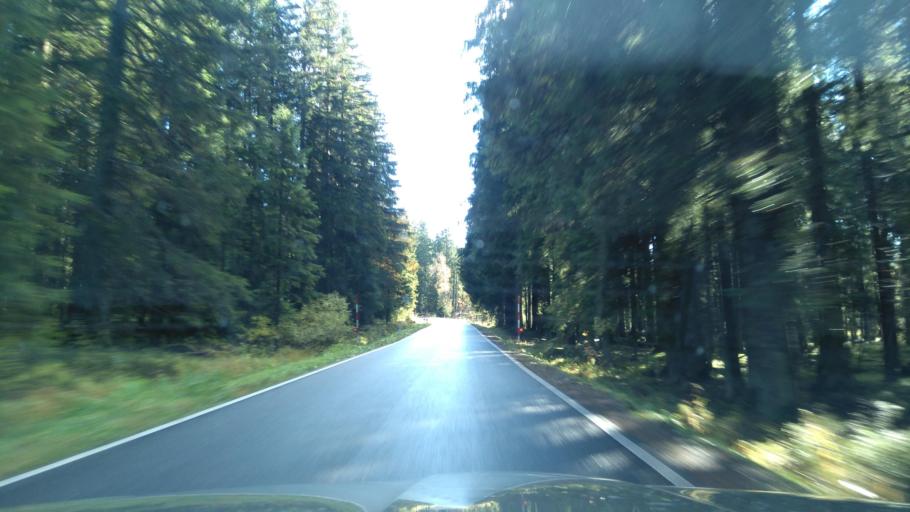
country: CZ
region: Plzensky
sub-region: Okres Klatovy
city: Kasperske Hory
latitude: 49.0280
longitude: 13.5311
